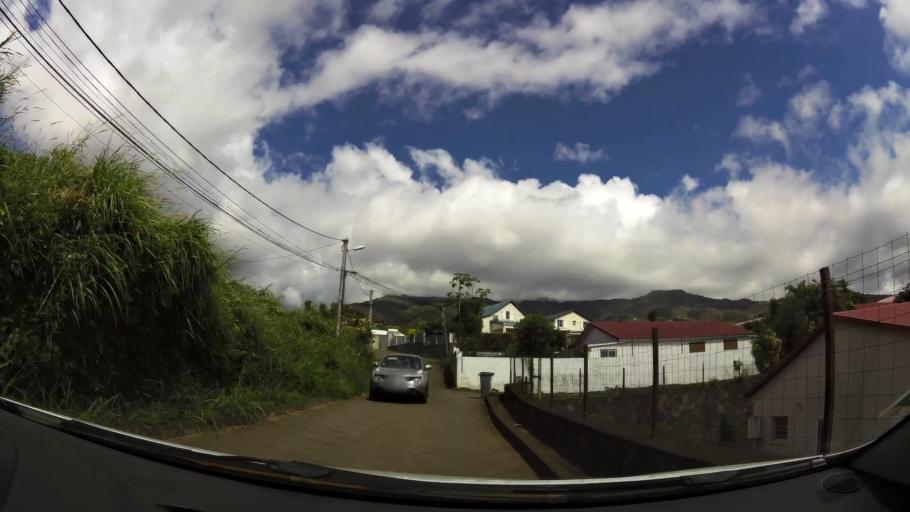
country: RE
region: Reunion
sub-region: Reunion
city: Sainte-Marie
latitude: -20.9269
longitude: 55.5000
